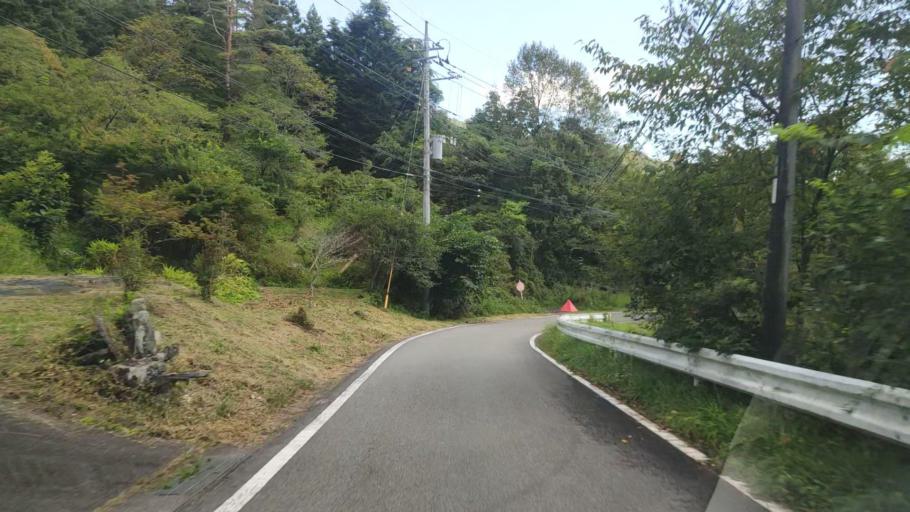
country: JP
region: Gunma
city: Nakanojomachi
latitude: 36.6574
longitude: 138.6295
